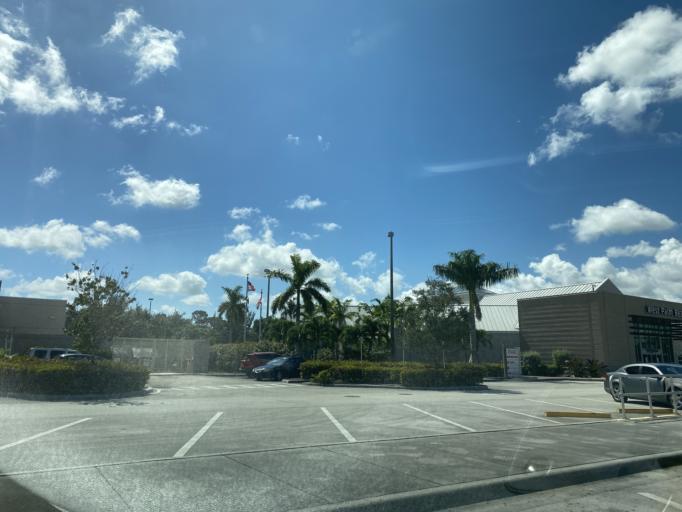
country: US
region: Florida
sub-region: Palm Beach County
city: Greenacres City
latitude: 26.6349
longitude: -80.1753
